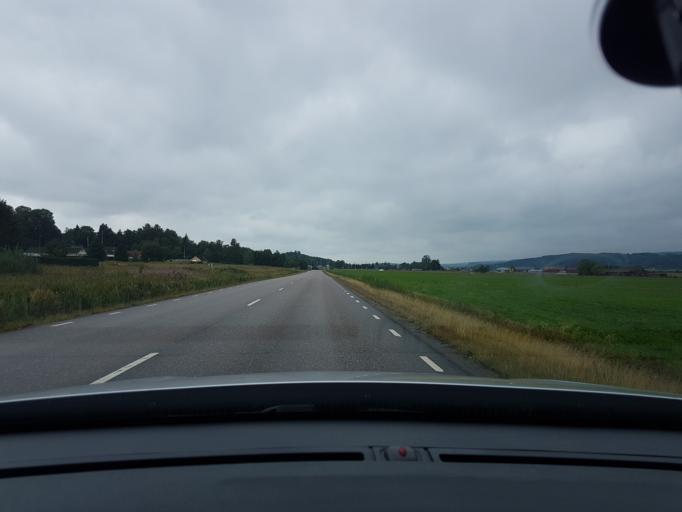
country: SE
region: Vaestra Goetaland
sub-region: Ale Kommun
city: Alvangen
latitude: 57.9694
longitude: 12.1596
